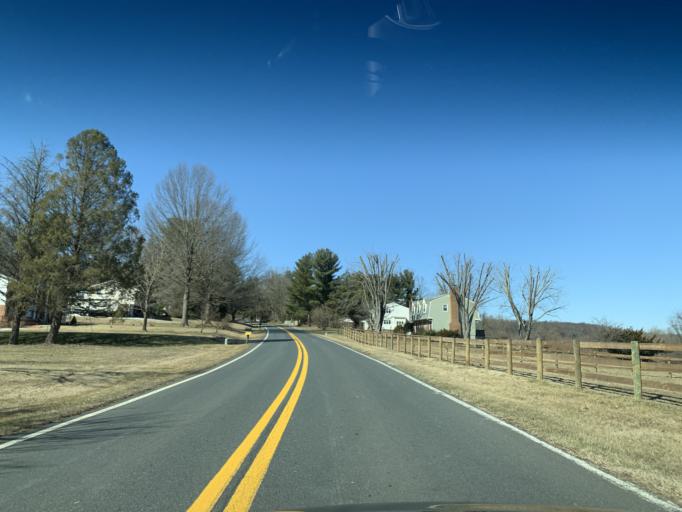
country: US
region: Maryland
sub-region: Carroll County
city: Hampstead
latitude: 39.5798
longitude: -76.8976
